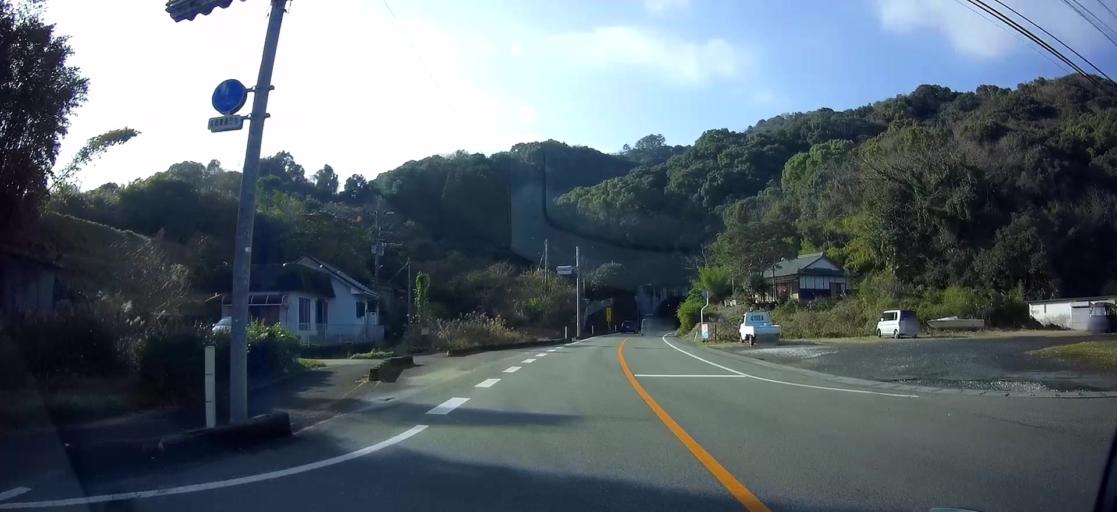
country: JP
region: Kumamoto
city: Yatsushiro
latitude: 32.4426
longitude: 130.4135
